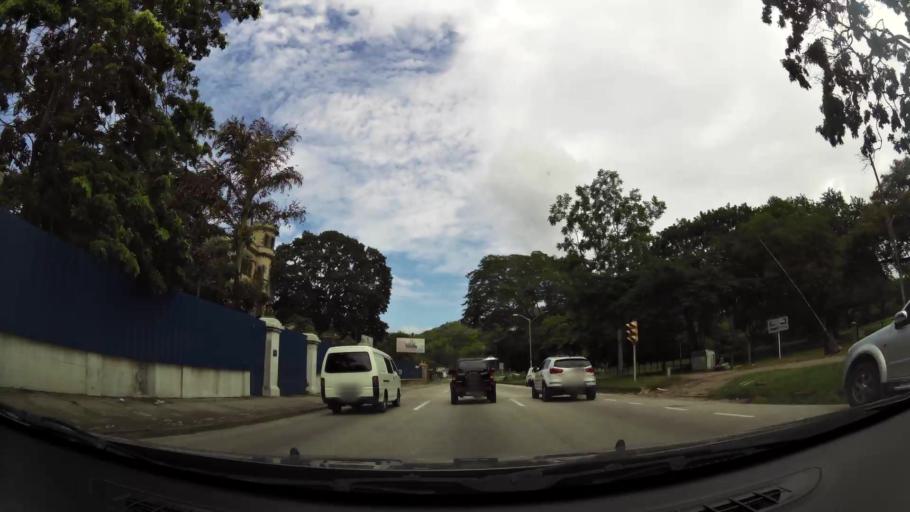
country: TT
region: City of Port of Spain
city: Port-of-Spain
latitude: 10.6721
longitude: -61.5186
